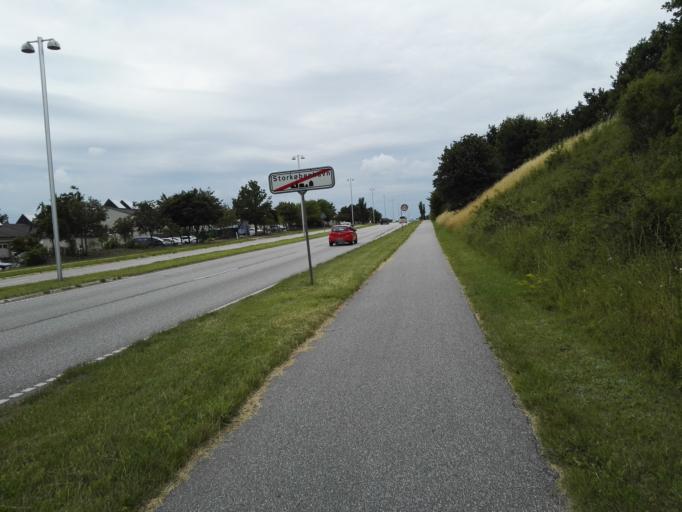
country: DK
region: Capital Region
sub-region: Egedal Kommune
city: Smorumnedre
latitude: 55.7514
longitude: 12.3072
